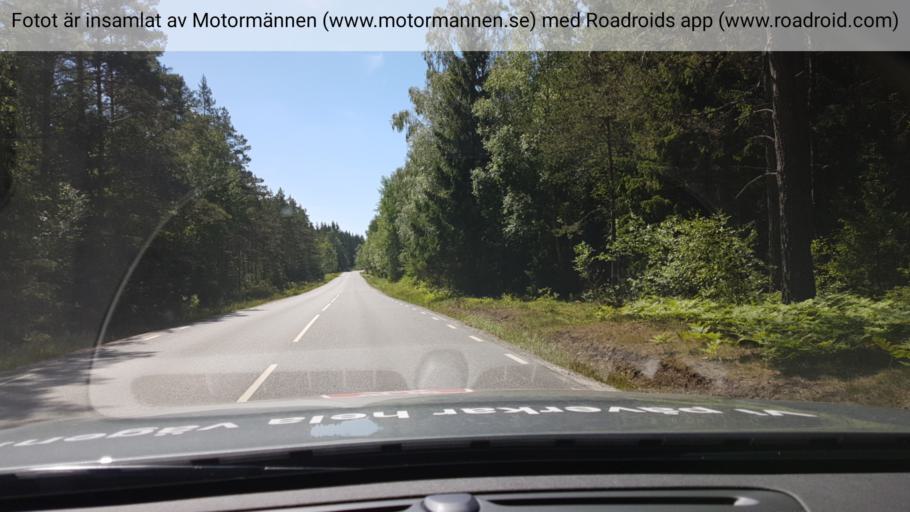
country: SE
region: Stockholm
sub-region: Haninge Kommun
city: Haninge
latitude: 59.1571
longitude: 18.1802
